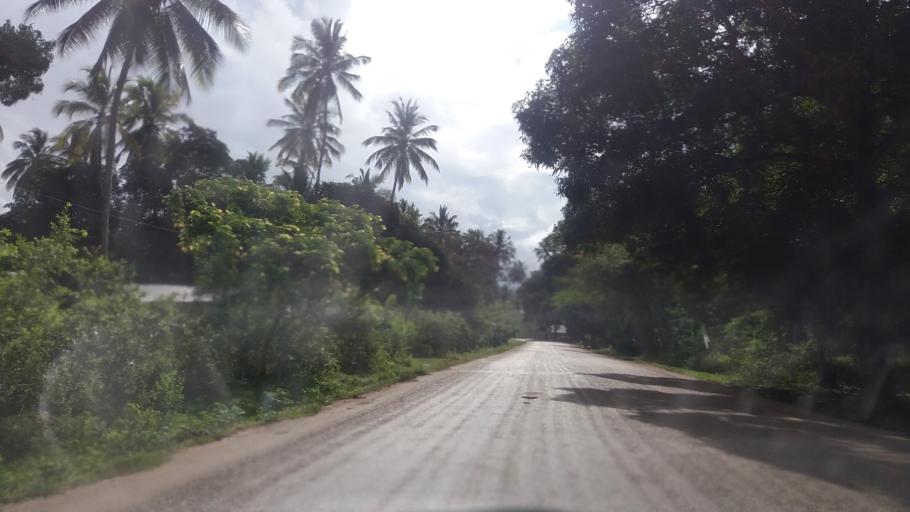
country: TZ
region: Zanzibar Central/South
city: Koani
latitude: -6.2027
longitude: 39.3225
